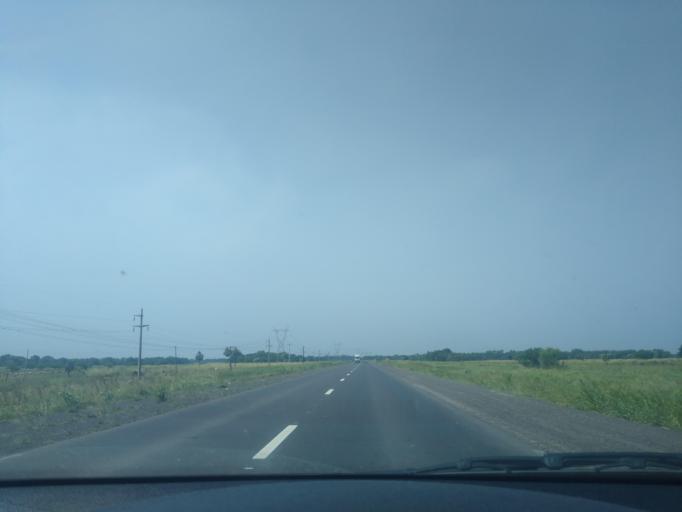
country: AR
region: Chaco
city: Fontana
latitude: -27.5660
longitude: -59.1523
